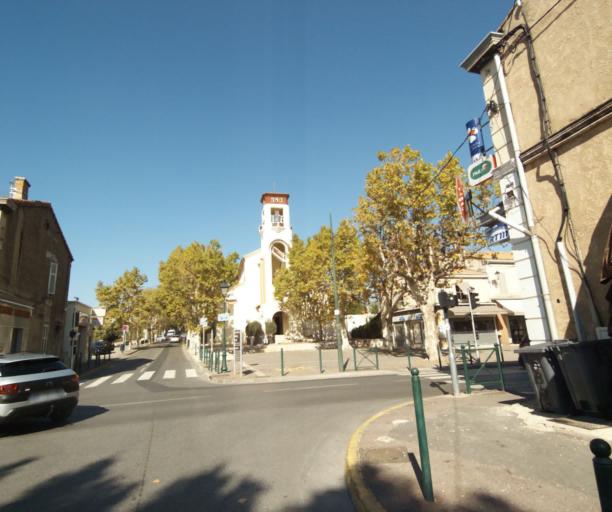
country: FR
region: Provence-Alpes-Cote d'Azur
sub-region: Departement des Bouches-du-Rhone
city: Plan-de-Cuques
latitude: 43.3474
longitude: 5.4638
